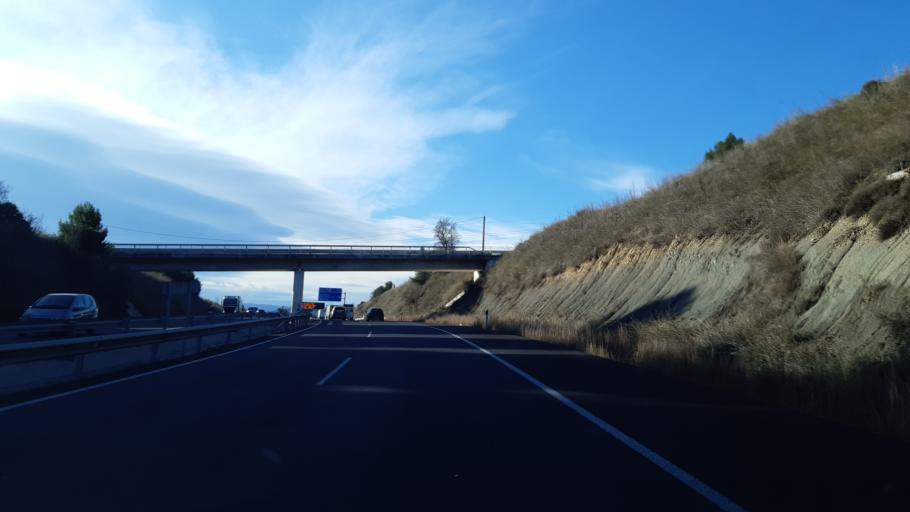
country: ES
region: Catalonia
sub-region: Provincia de Barcelona
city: Castelloli
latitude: 41.5943
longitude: 1.6812
